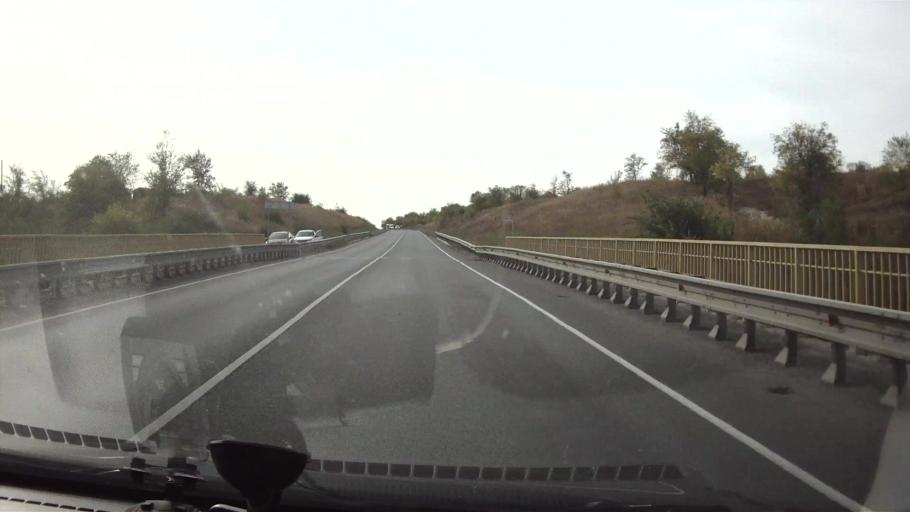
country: RU
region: Saratov
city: Tersa
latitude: 52.0853
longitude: 47.5899
